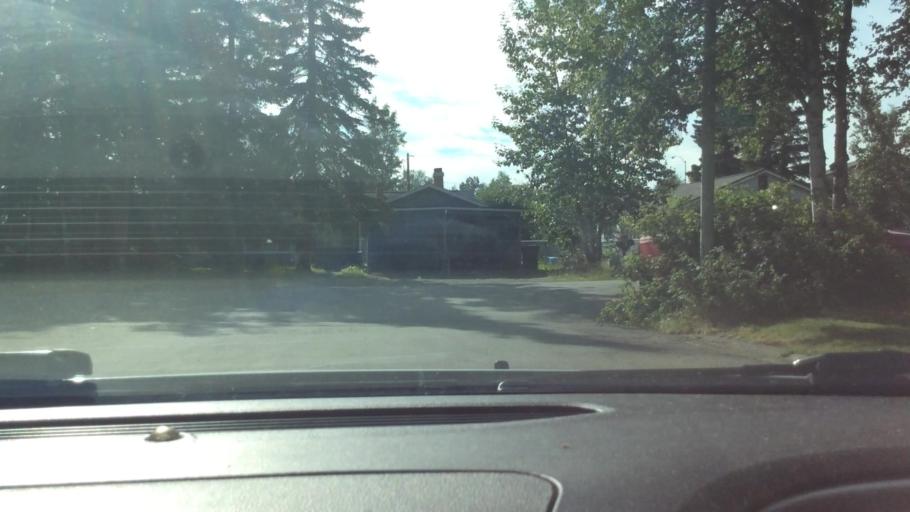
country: US
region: Alaska
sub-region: Anchorage Municipality
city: Anchorage
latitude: 61.1969
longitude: -149.7757
